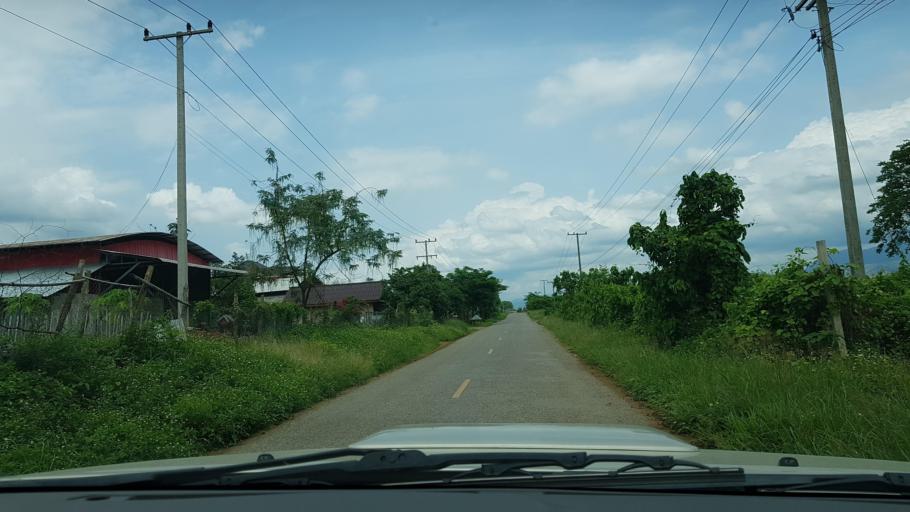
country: TH
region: Nan
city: Chaloem Phra Kiat
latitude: 20.0029
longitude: 101.2954
